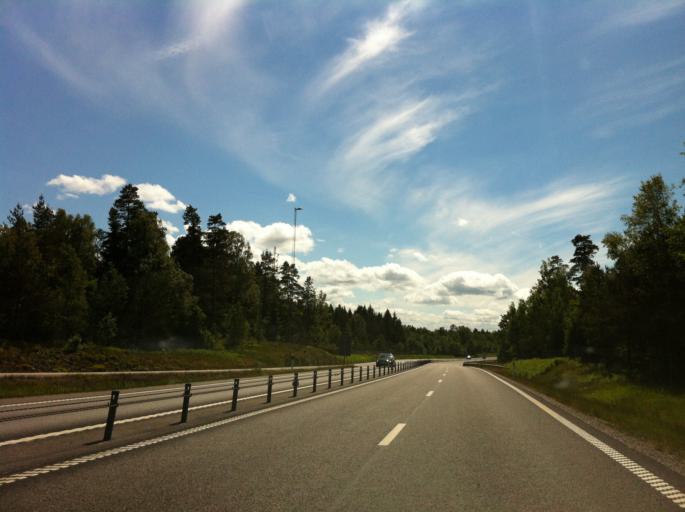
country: SE
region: Vaestra Goetaland
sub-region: Vanersborgs Kommun
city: Vanersborg
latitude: 58.3877
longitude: 12.2890
